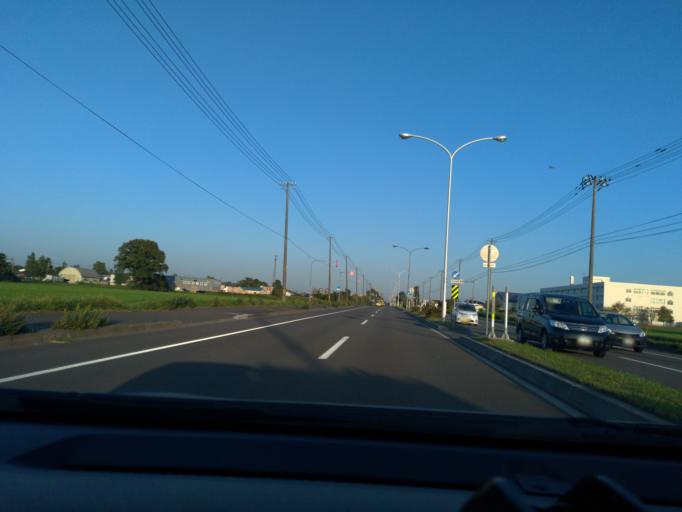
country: JP
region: Hokkaido
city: Ishikari
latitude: 43.1609
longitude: 141.3669
